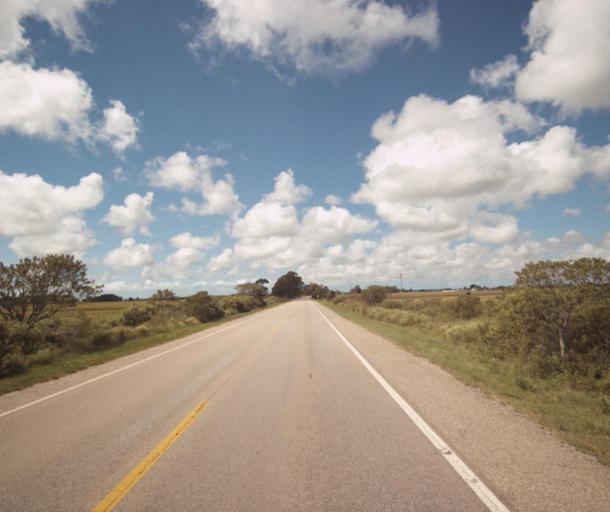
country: BR
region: Rio Grande do Sul
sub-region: Arroio Grande
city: Arroio Grande
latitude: -32.5296
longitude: -52.5427
